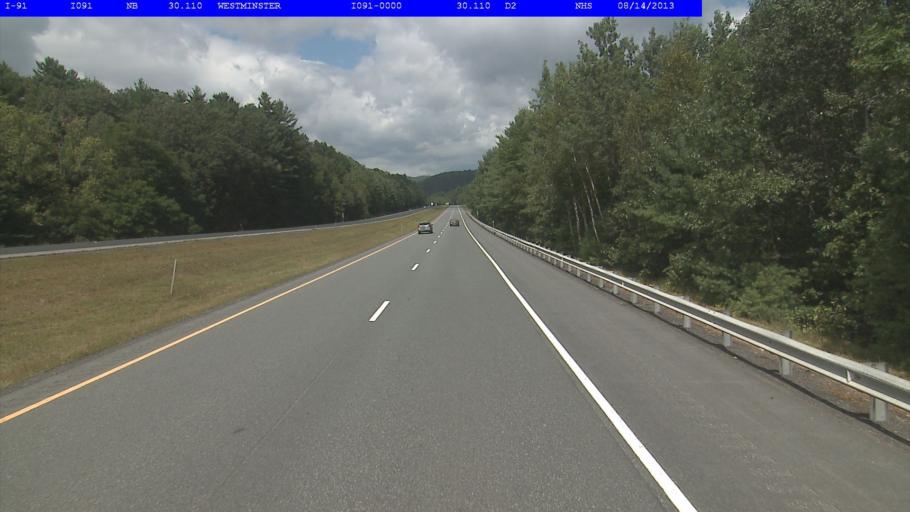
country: US
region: Vermont
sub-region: Windham County
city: Bellows Falls
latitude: 43.1120
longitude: -72.4578
